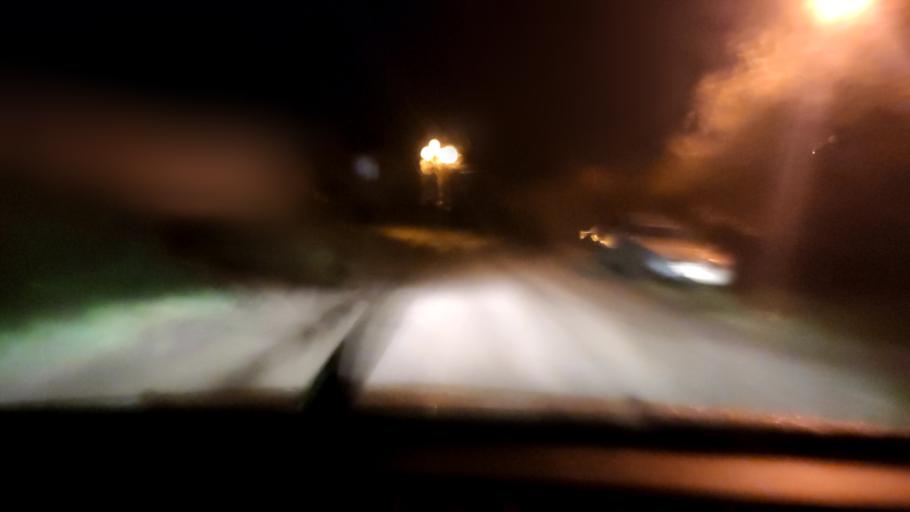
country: RU
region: Voronezj
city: Pridonskoy
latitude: 51.6167
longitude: 39.0642
